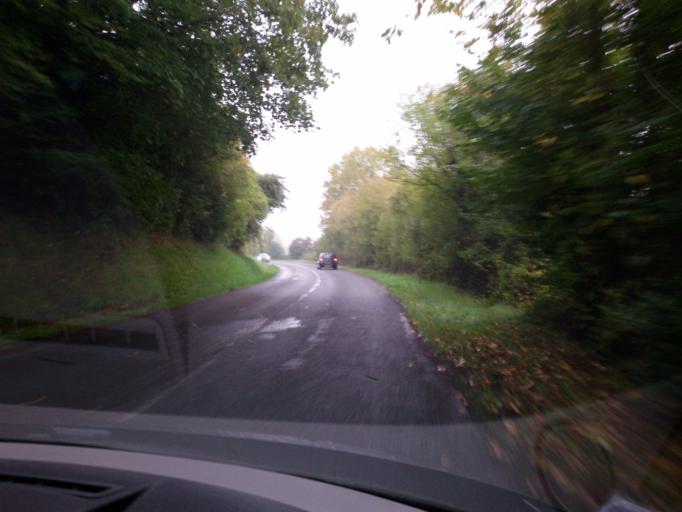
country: FR
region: Lower Normandy
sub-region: Departement du Calvados
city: Ablon
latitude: 49.4296
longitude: 0.3432
